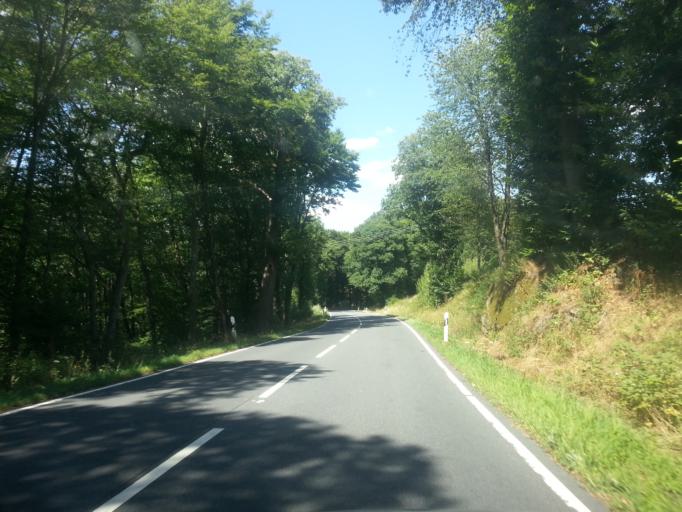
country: DE
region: Hesse
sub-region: Regierungsbezirk Darmstadt
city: Frankisch-Crumbach
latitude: 49.7180
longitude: 8.8881
